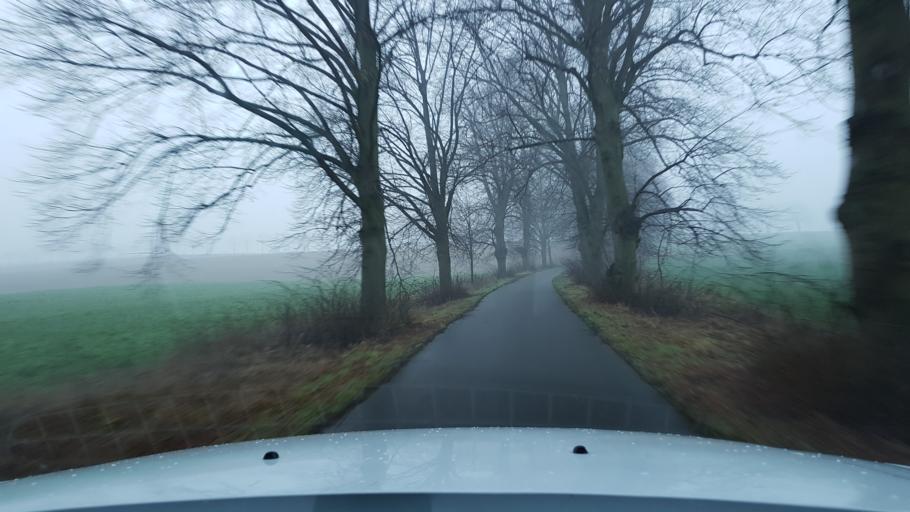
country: DE
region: Brandenburg
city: Mescherin
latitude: 53.2764
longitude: 14.4103
